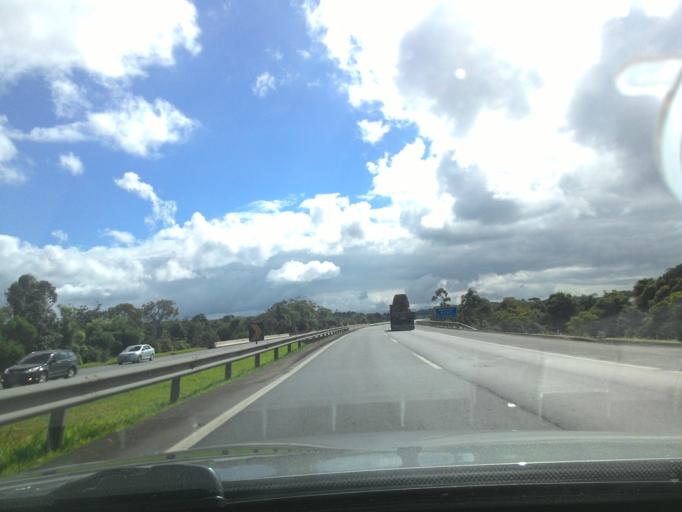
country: BR
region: Sao Paulo
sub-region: Cajati
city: Cajati
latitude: -24.9303
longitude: -48.2754
